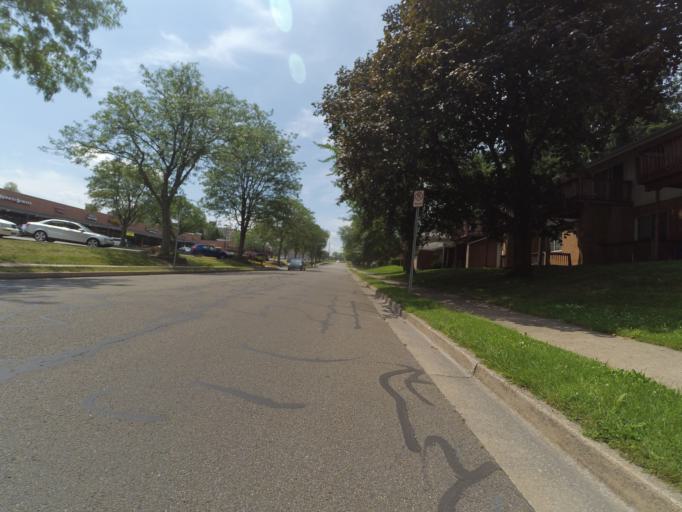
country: US
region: Pennsylvania
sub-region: Centre County
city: State College
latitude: 40.7884
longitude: -77.8562
